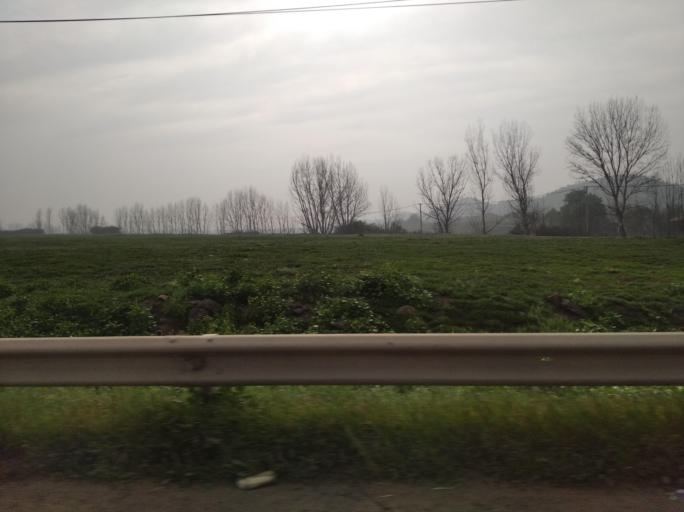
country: CL
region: Santiago Metropolitan
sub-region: Provincia de Chacabuco
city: Lampa
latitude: -33.3494
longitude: -70.8051
